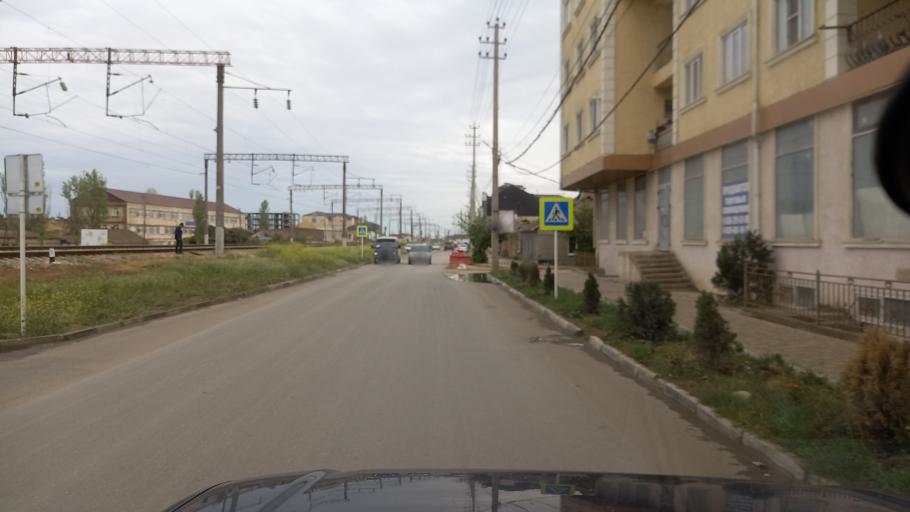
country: RU
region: Dagestan
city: Derbent
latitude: 42.0689
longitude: 48.3002
